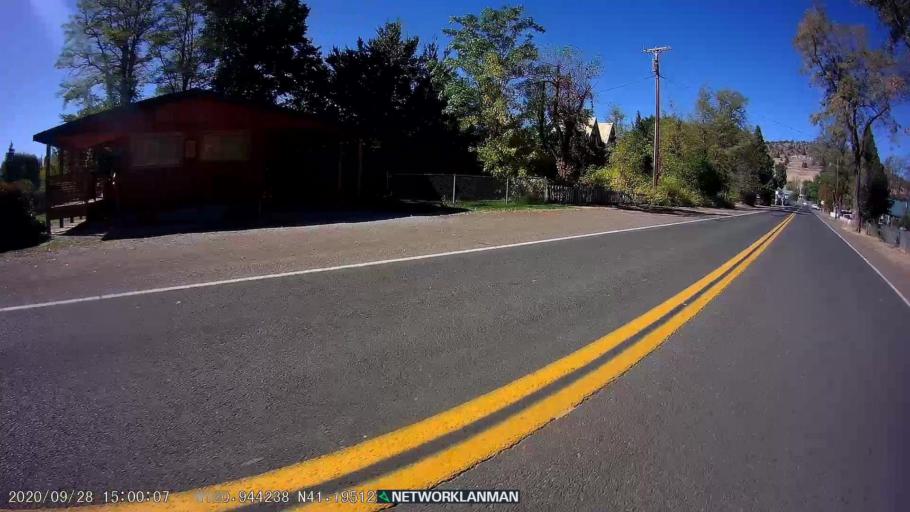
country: US
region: California
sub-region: Modoc County
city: Alturas
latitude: 41.1955
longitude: -120.9442
